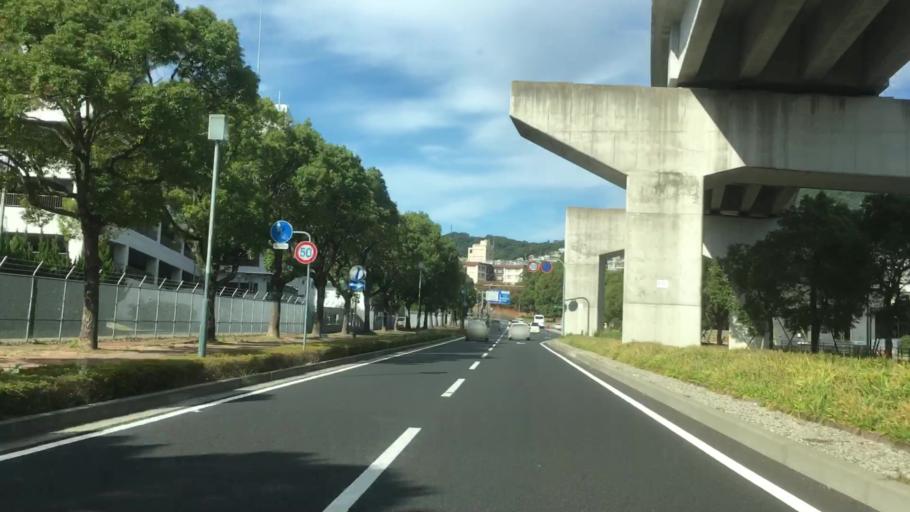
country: JP
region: Nagasaki
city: Sasebo
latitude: 33.1686
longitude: 129.7168
